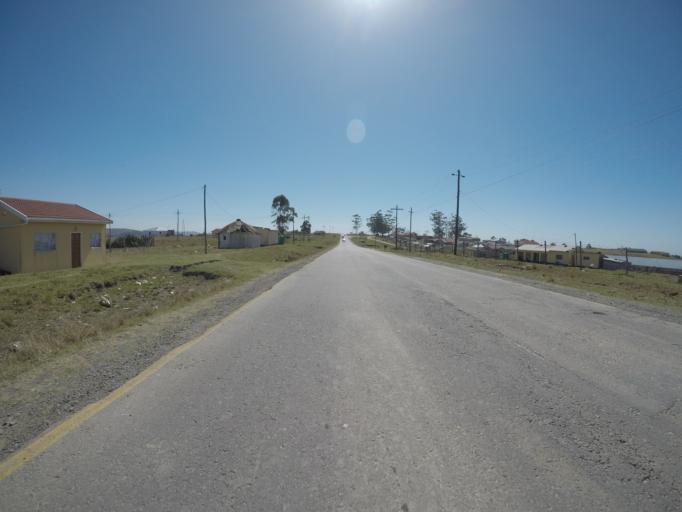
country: ZA
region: Eastern Cape
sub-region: OR Tambo District Municipality
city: Libode
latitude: -31.9196
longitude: 28.9753
